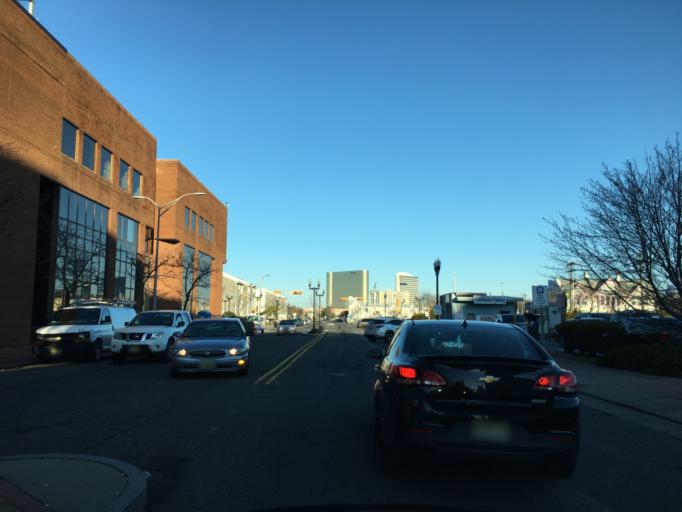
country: US
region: New Jersey
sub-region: Atlantic County
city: Atlantic City
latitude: 39.3640
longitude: -74.4261
